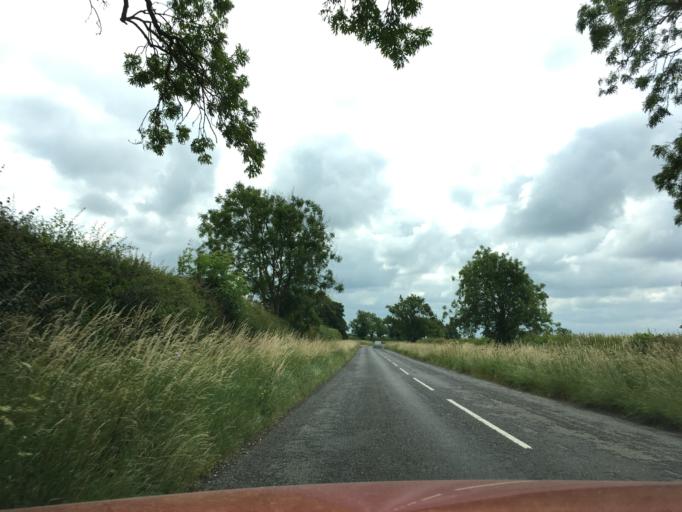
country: GB
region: England
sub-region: Oxfordshire
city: Charlbury
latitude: 51.9153
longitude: -1.4944
